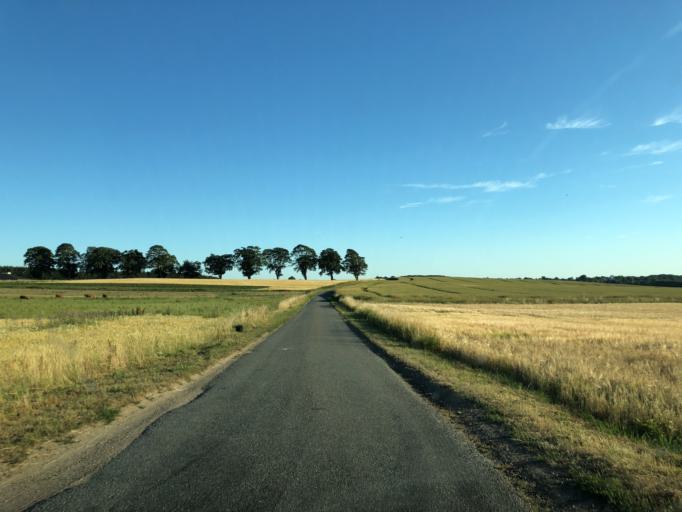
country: DK
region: Central Jutland
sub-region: Horsens Kommune
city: Horsens
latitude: 55.9033
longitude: 9.8635
